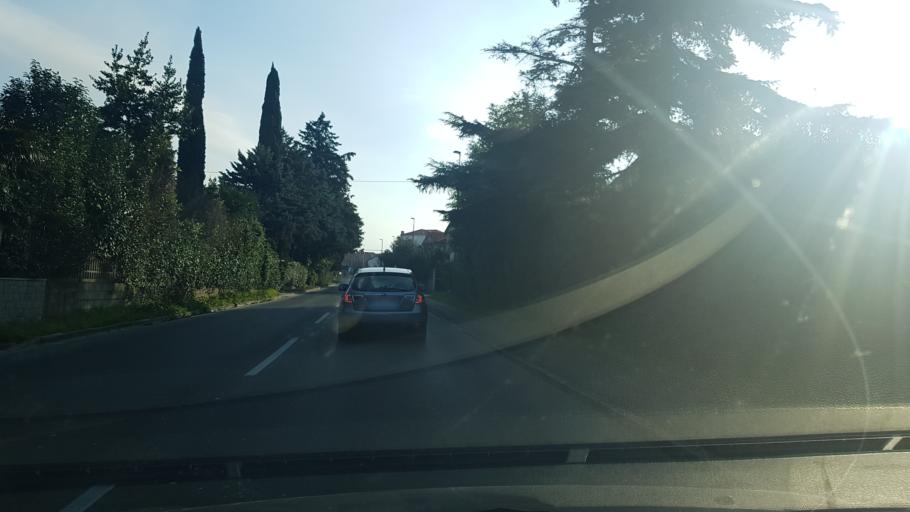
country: SI
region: Koper-Capodistria
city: Prade
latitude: 45.5413
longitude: 13.7691
